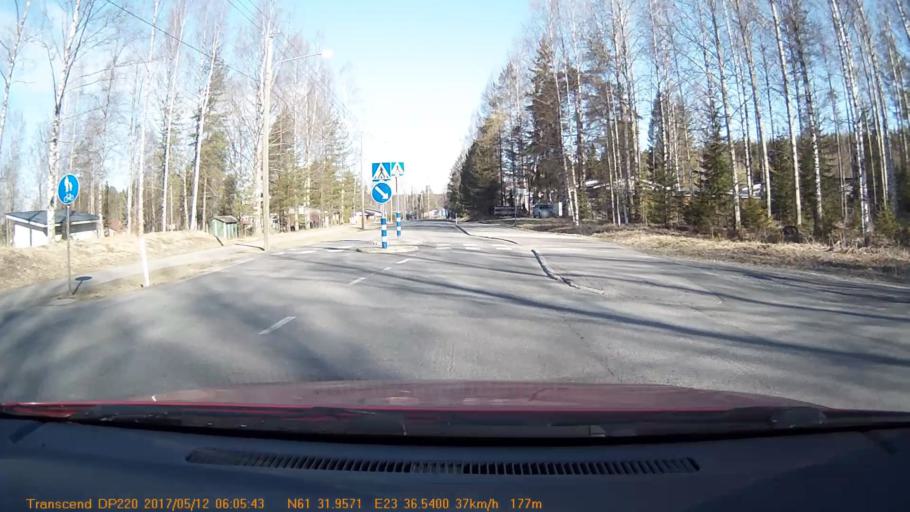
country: FI
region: Pirkanmaa
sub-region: Tampere
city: Yloejaervi
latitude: 61.5325
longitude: 23.6091
